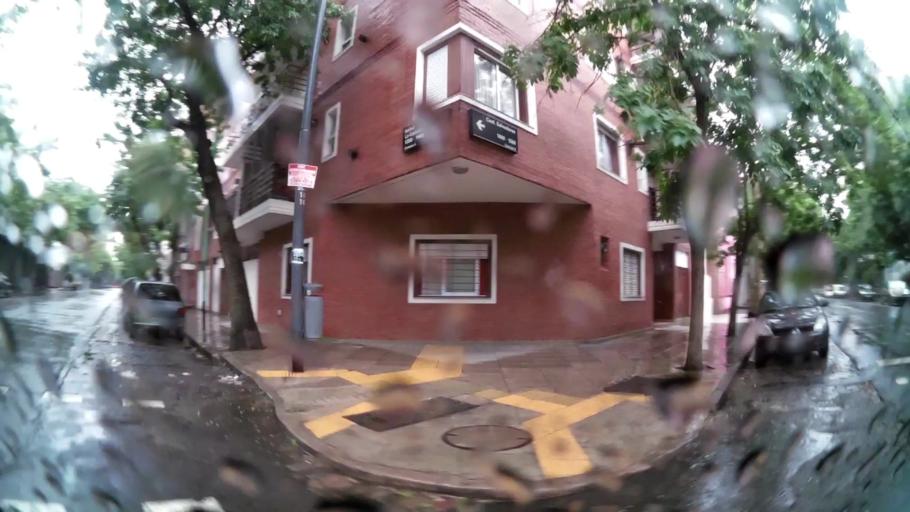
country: AR
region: Buenos Aires
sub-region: Partido de Avellaneda
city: Avellaneda
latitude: -34.6454
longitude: -58.3720
